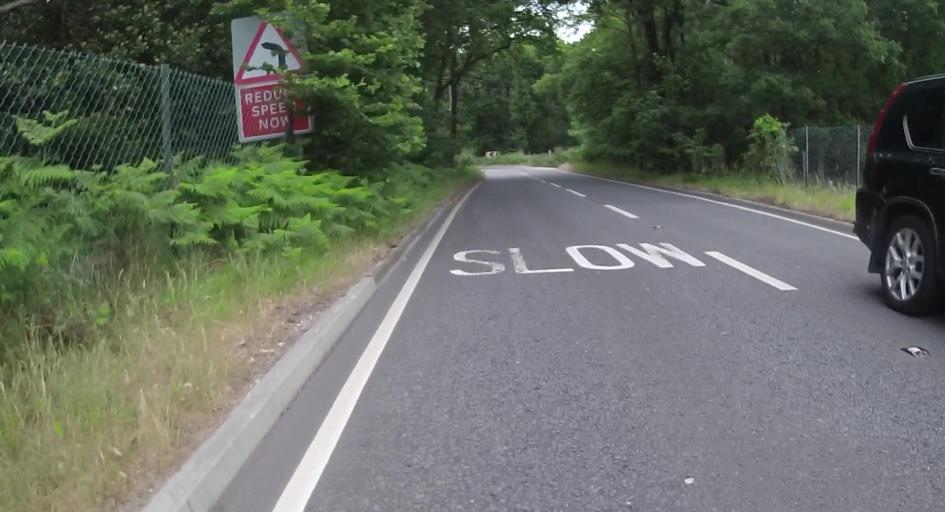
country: GB
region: England
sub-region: Hampshire
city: Fleet
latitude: 51.2604
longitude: -0.8234
